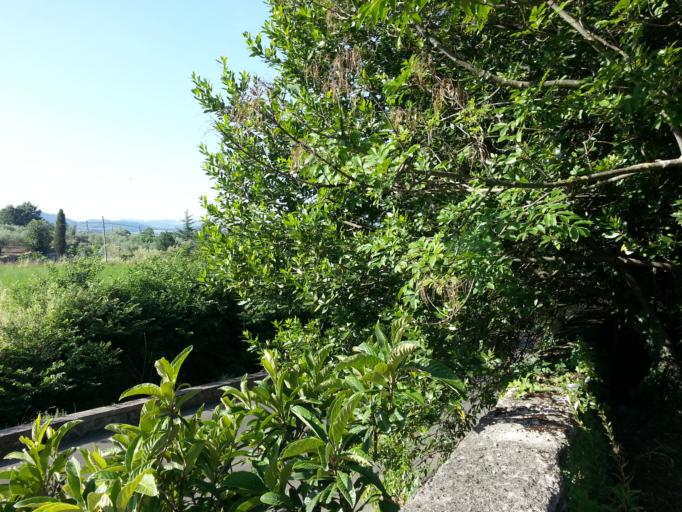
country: IT
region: Latium
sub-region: Provincia di Viterbo
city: Bolsena
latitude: 42.6461
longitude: 11.9932
